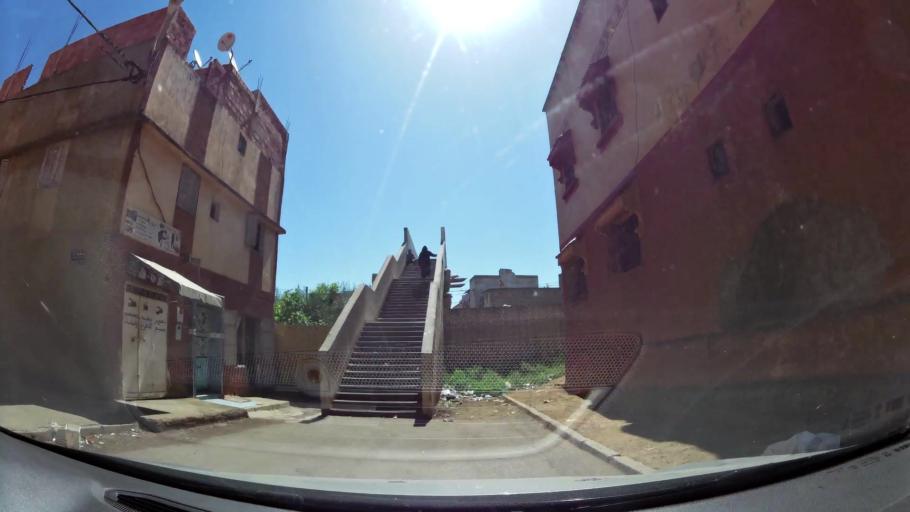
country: MA
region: Meknes-Tafilalet
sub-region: Meknes
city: Meknes
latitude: 33.9081
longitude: -5.5367
